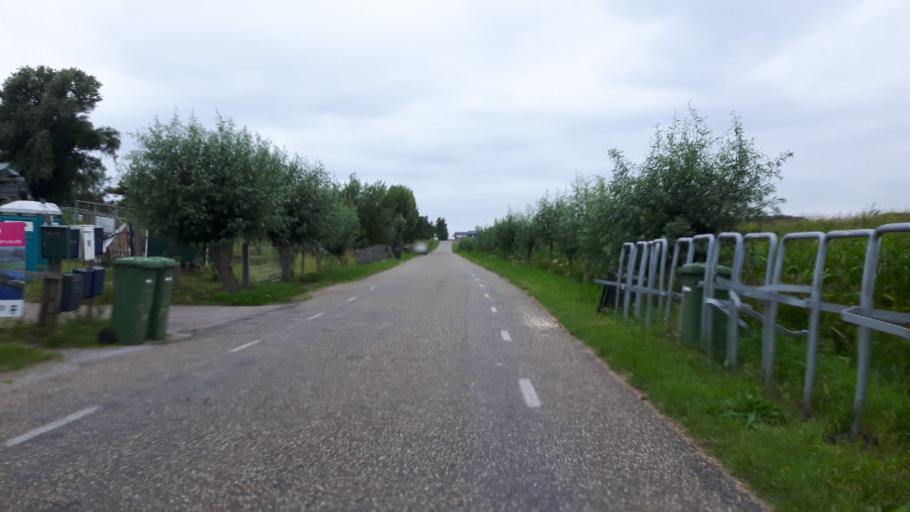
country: NL
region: South Holland
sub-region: Gemeente Kaag en Braassem
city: Oude Wetering
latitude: 52.2086
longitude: 4.6569
